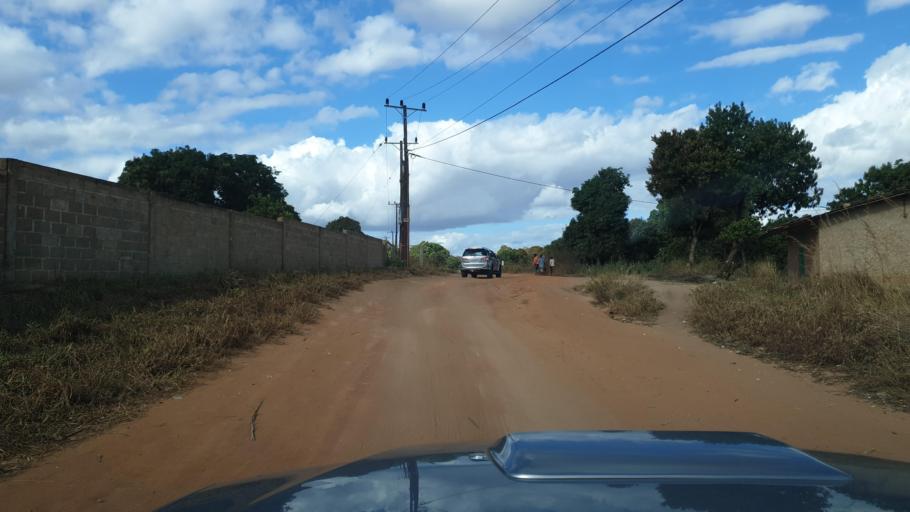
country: ER
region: Debub
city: Dek'emhare
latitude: 15.0815
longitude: 39.2035
